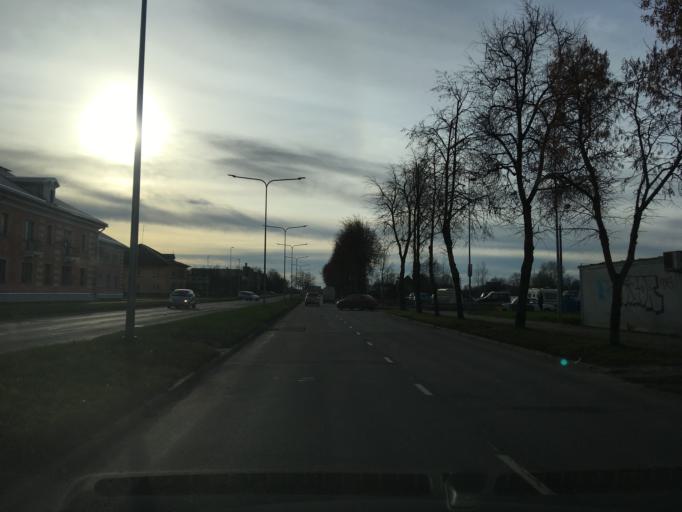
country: EE
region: Ida-Virumaa
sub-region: Narva linn
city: Narva
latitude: 59.3642
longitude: 28.1880
